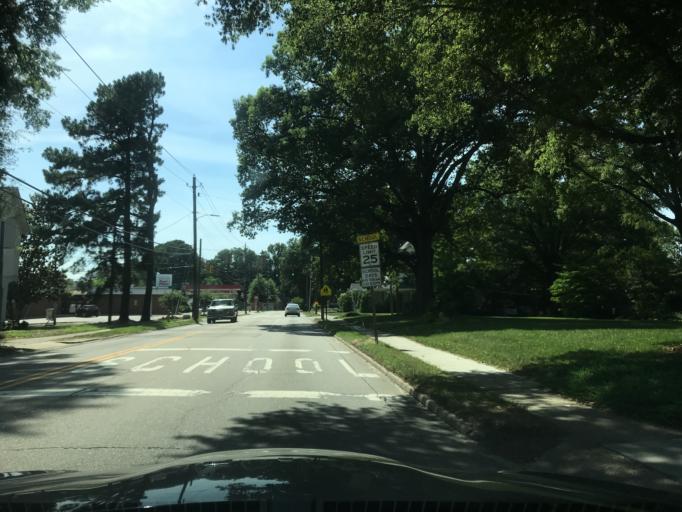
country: US
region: North Carolina
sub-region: Wake County
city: Wendell
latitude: 35.7845
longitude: -78.3702
